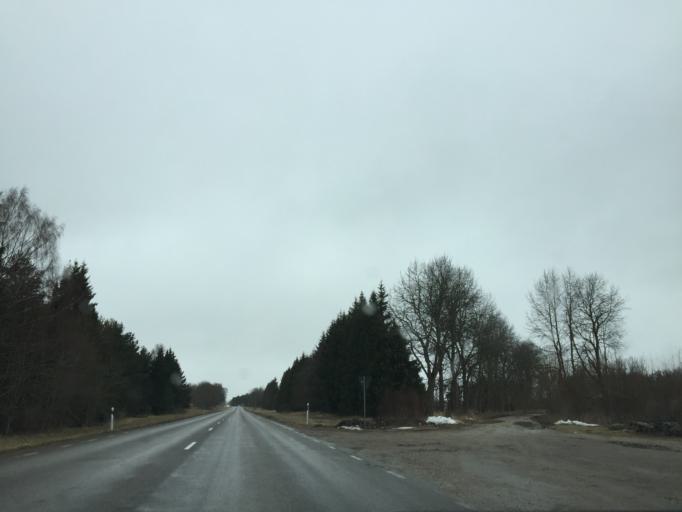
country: EE
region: Laeaene
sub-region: Ridala Parish
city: Uuemoisa
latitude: 58.8749
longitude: 23.6124
